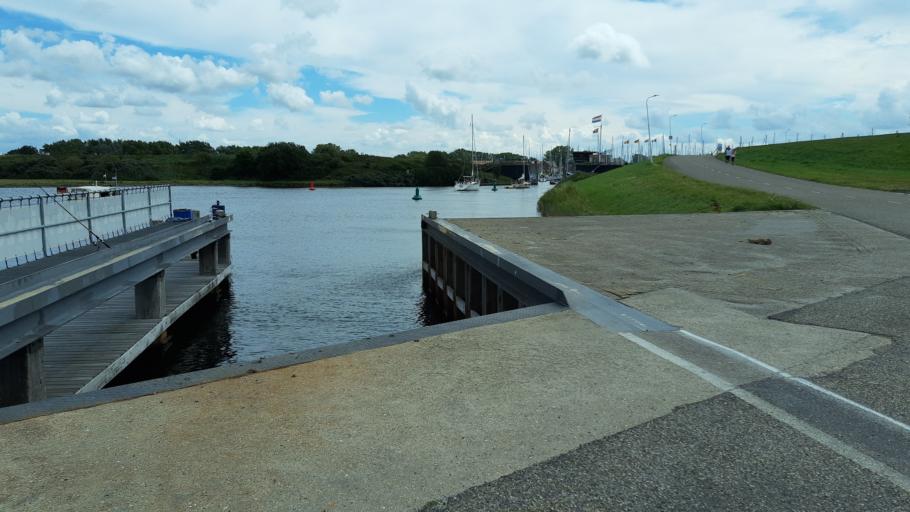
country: NL
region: Zeeland
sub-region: Schouwen-Duiveland
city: Scharendijke
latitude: 51.7315
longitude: 3.9118
